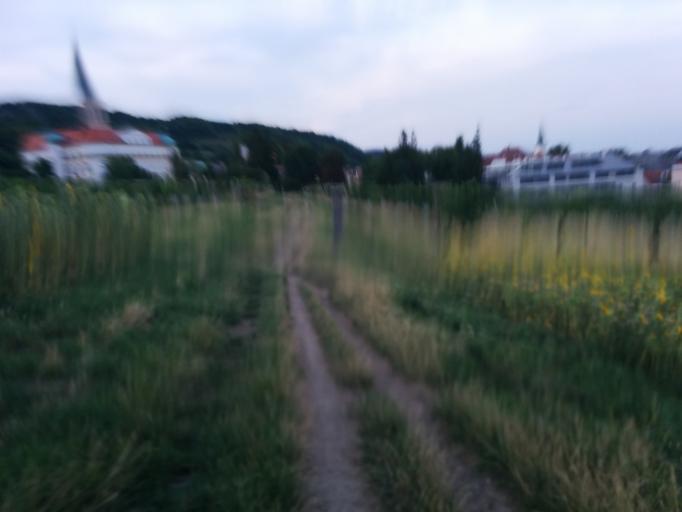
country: AT
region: Lower Austria
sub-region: Politischer Bezirk Modling
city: Gumpoldskirchen
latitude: 48.0440
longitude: 16.2736
